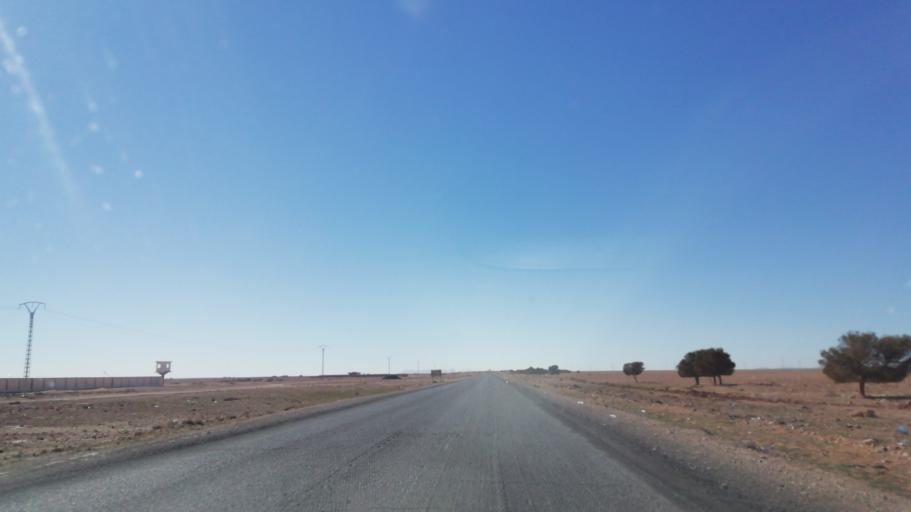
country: DZ
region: Saida
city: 'Ain el Hadjar
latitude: 34.0200
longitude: 0.0632
